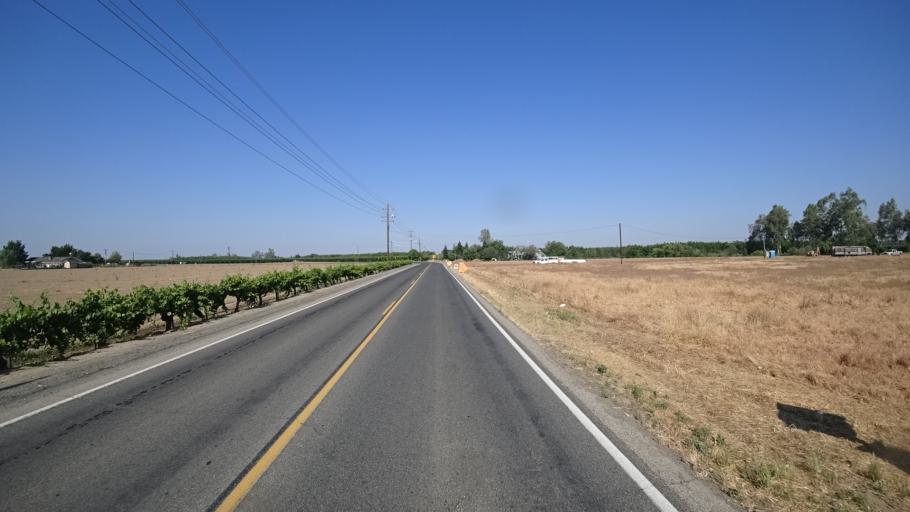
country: US
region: California
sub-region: Fresno County
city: Kingsburg
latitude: 36.4813
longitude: -119.5619
